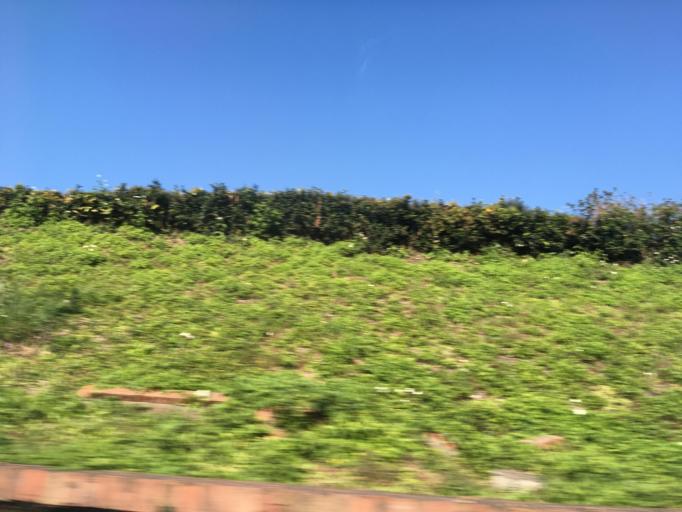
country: TW
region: Taiwan
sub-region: Yilan
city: Yilan
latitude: 24.7571
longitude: 121.7442
